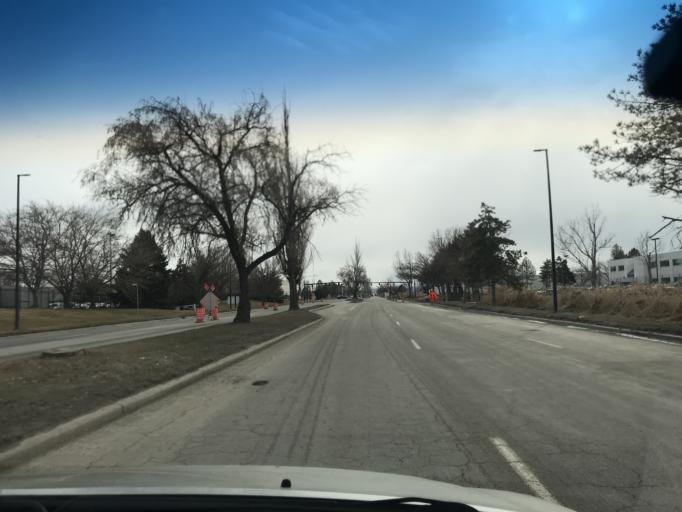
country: US
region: Utah
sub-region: Salt Lake County
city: West Valley City
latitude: 40.7835
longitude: -112.0251
